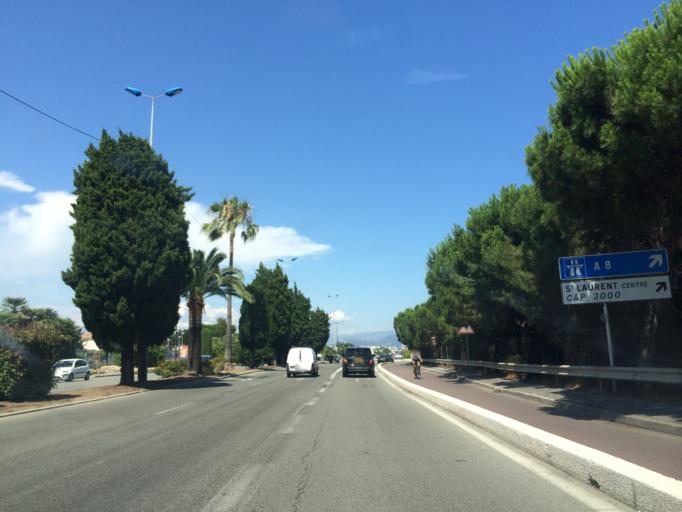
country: FR
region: Provence-Alpes-Cote d'Azur
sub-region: Departement des Alpes-Maritimes
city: Saint-Laurent-du-Var
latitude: 43.6620
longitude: 7.1952
